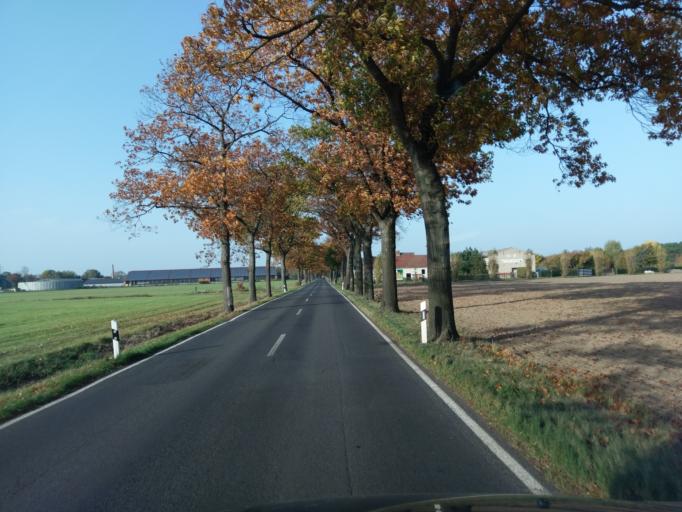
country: DE
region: Brandenburg
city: Herzberg
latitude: 51.6530
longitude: 13.2346
